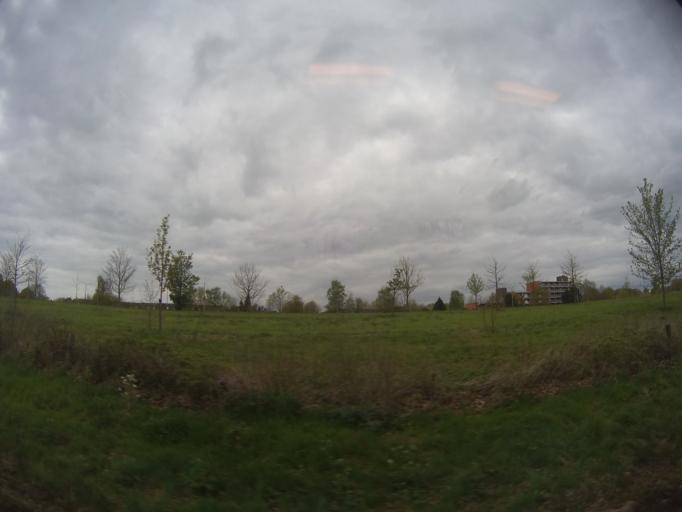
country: NL
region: Drenthe
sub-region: Gemeente Emmen
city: Emmen
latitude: 52.7691
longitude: 6.8982
